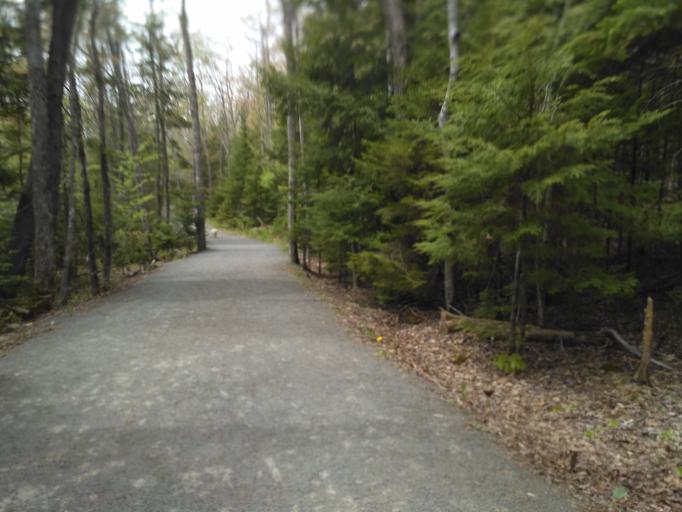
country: CA
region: Nova Scotia
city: Dartmouth
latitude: 44.7680
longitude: -63.6519
